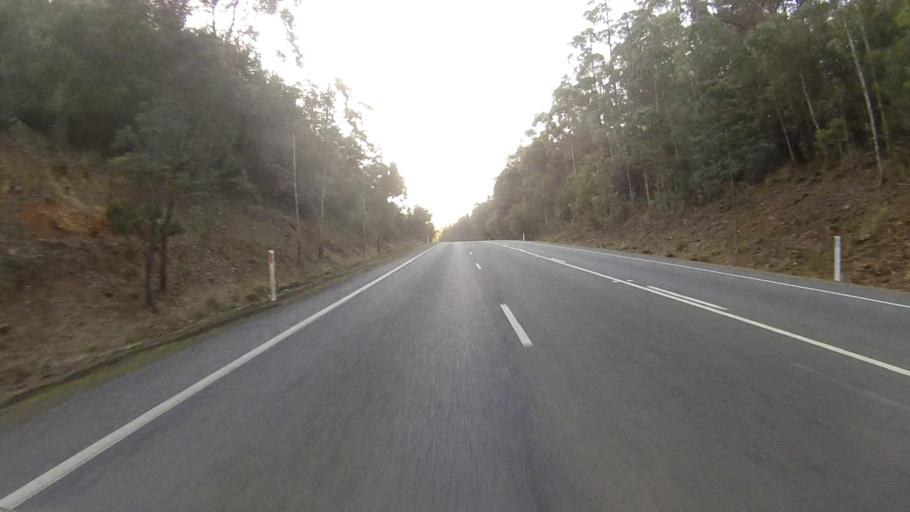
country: AU
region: Tasmania
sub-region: Sorell
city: Sorell
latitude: -43.0024
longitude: 147.9267
